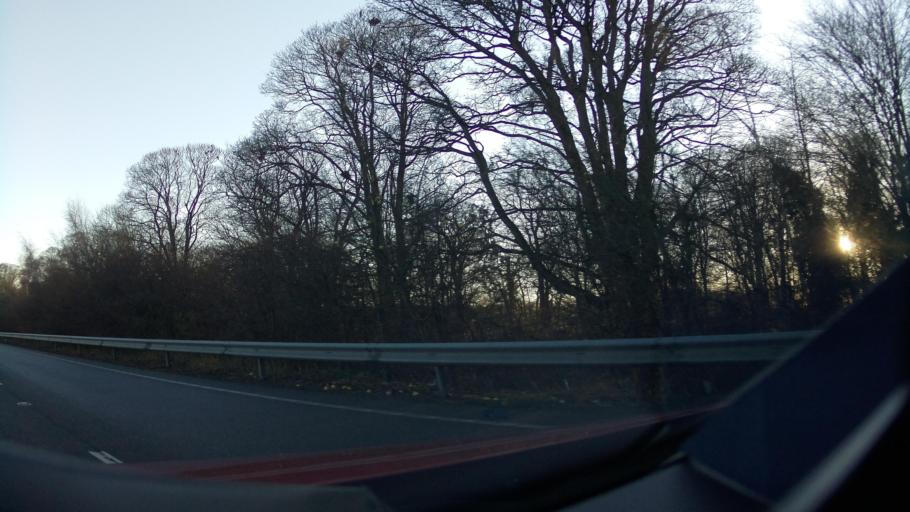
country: GB
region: England
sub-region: North Yorkshire
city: Catterick Garrison
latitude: 54.4482
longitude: -1.6881
